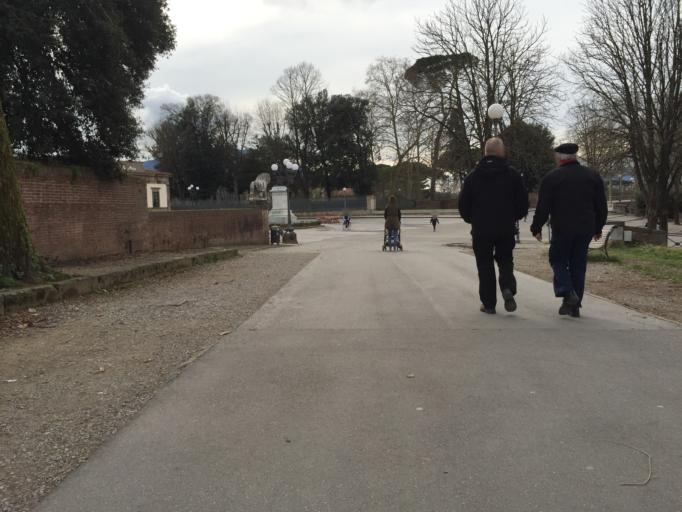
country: IT
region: Tuscany
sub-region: Provincia di Lucca
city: Lucca
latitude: 43.8389
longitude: 10.5024
